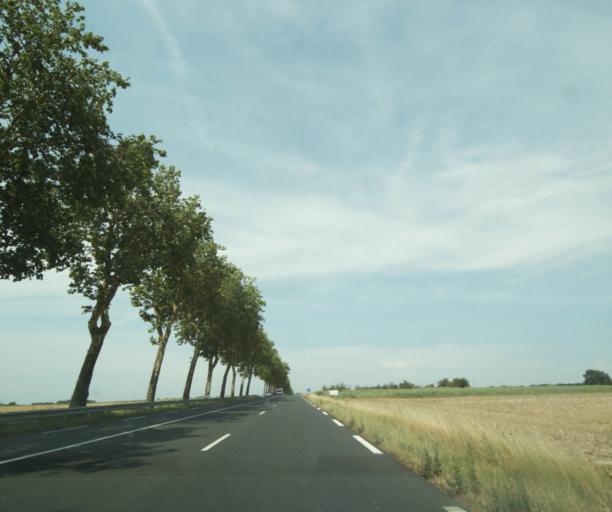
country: FR
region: Centre
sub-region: Departement d'Indre-et-Loire
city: Sainte-Maure-de-Touraine
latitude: 47.1221
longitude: 0.6244
